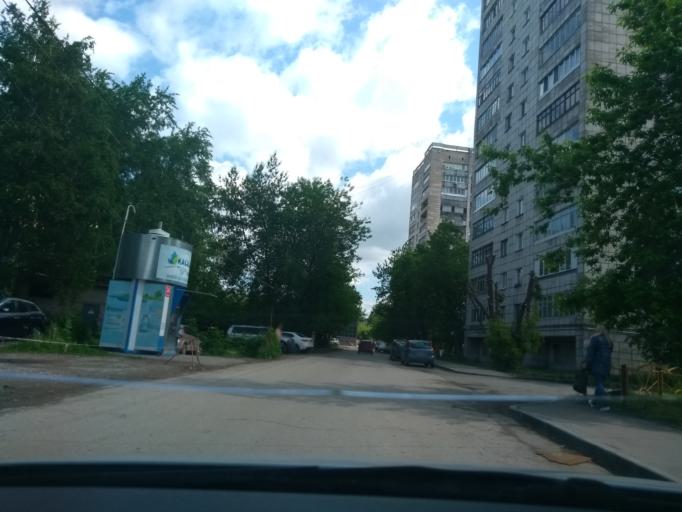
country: RU
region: Perm
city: Perm
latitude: 57.9924
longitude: 56.1974
